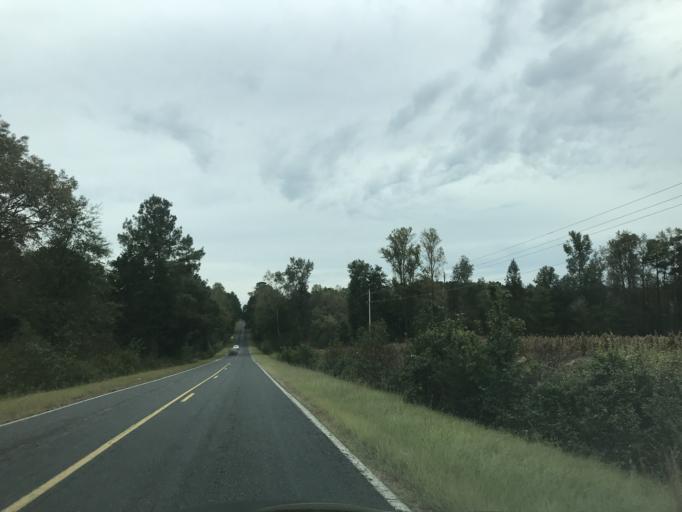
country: US
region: North Carolina
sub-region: Wake County
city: Knightdale
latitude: 35.8296
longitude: -78.4897
